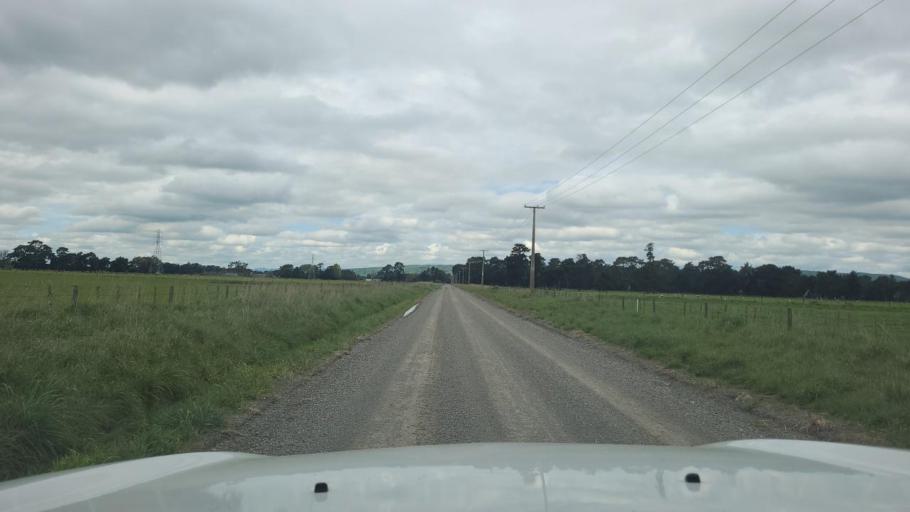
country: NZ
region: Wellington
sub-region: Masterton District
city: Masterton
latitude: -41.1190
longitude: 175.4224
